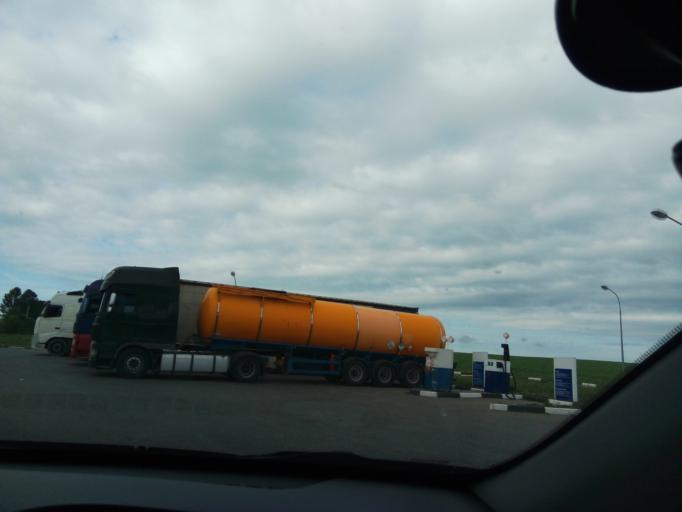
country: RU
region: Rjazan
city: Shatsk
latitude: 53.9845
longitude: 41.7088
